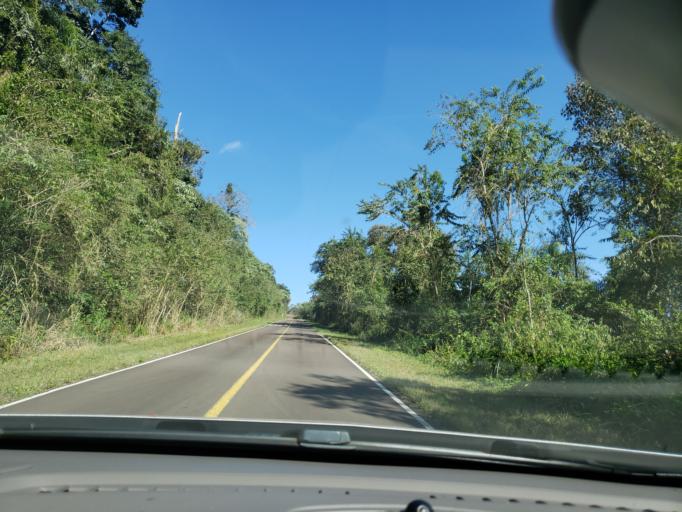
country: BR
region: Rio Grande do Sul
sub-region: Tres Passos
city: Tres Passos
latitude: -27.1494
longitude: -53.9114
